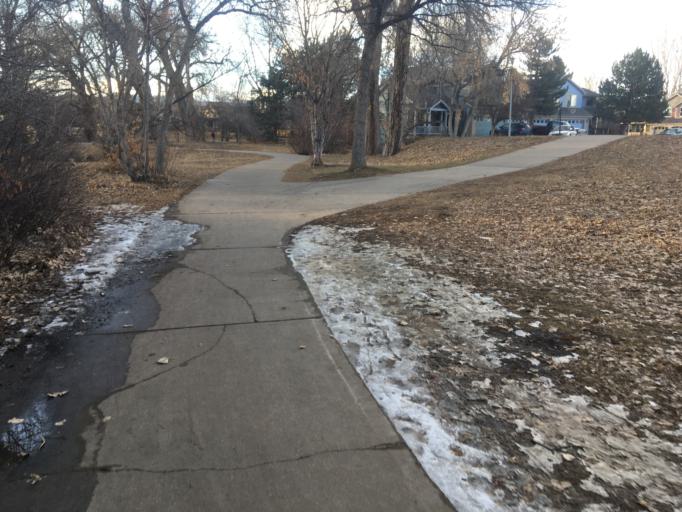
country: US
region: Colorado
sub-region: Jefferson County
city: Applewood
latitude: 39.8222
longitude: -105.1589
